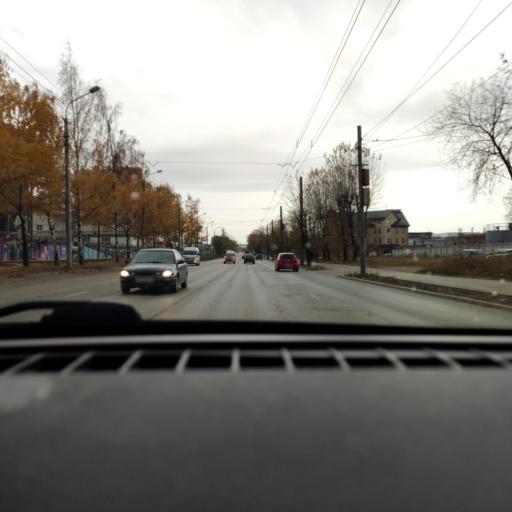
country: RU
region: Perm
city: Perm
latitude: 57.9788
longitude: 56.2466
